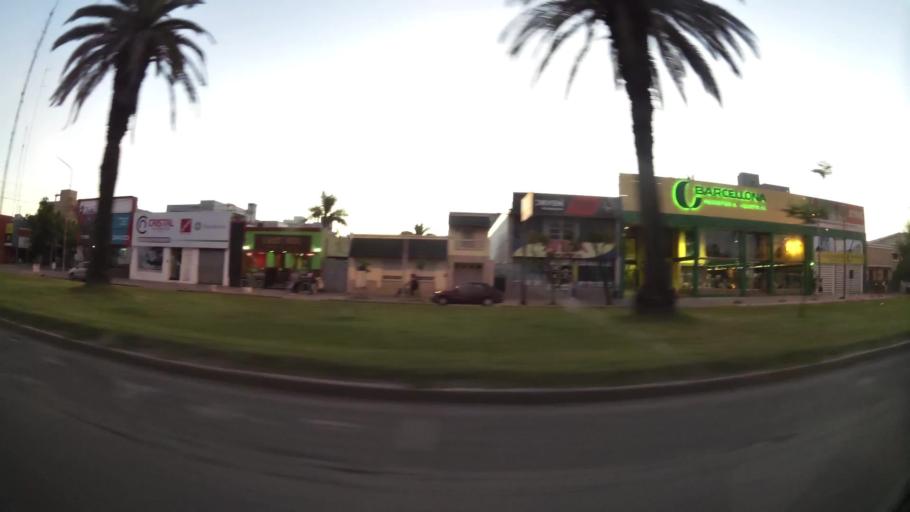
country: AR
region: Cordoba
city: Villa Maria
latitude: -32.4069
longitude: -63.2402
